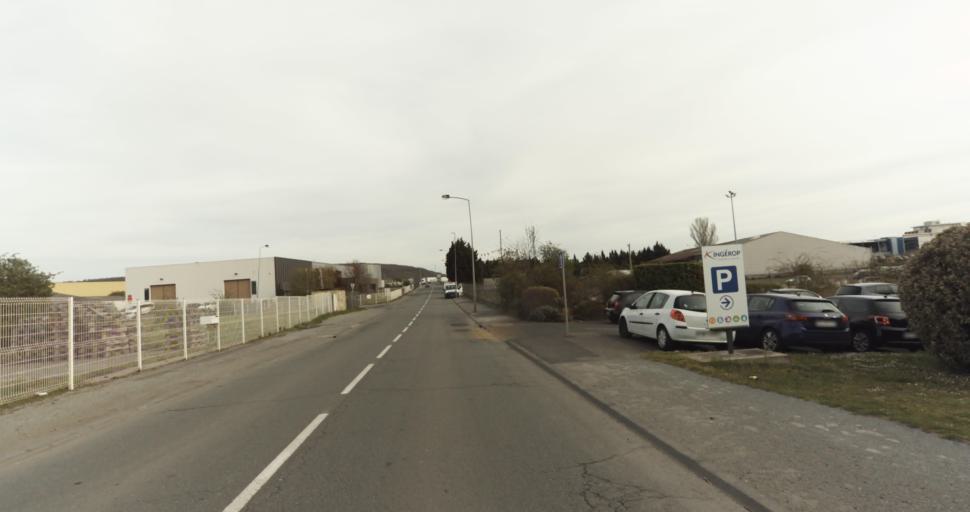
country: FR
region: Auvergne
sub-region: Departement du Puy-de-Dome
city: Cebazat
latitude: 45.8391
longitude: 3.1178
